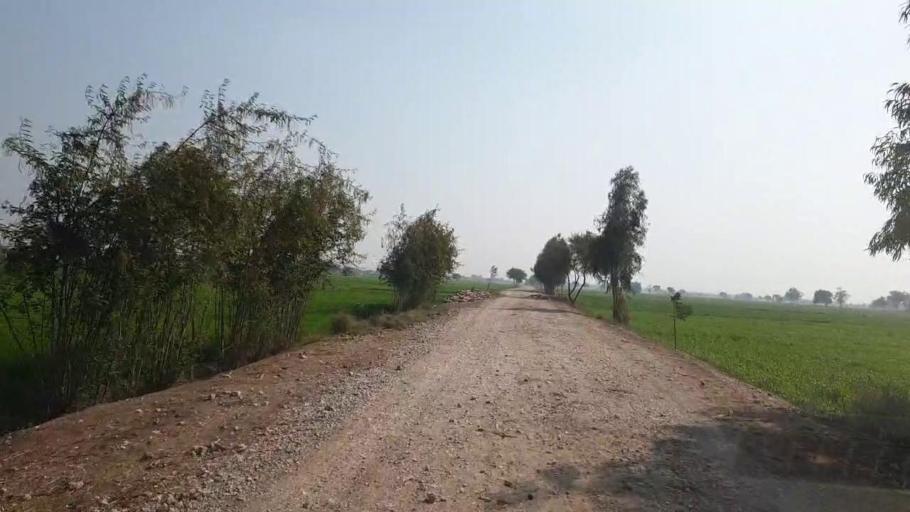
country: PK
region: Sindh
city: Bhit Shah
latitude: 25.7362
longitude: 68.5245
